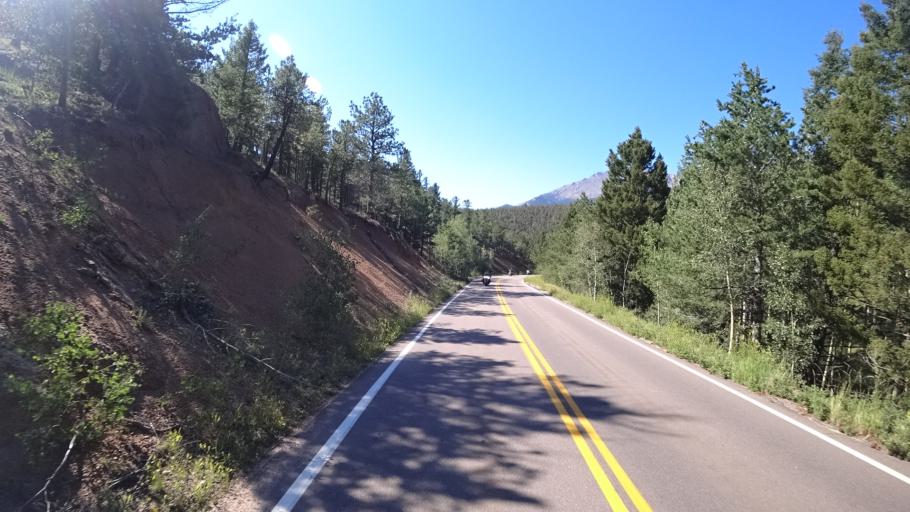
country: US
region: Colorado
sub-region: El Paso County
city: Cascade-Chipita Park
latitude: 38.9071
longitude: -105.0127
